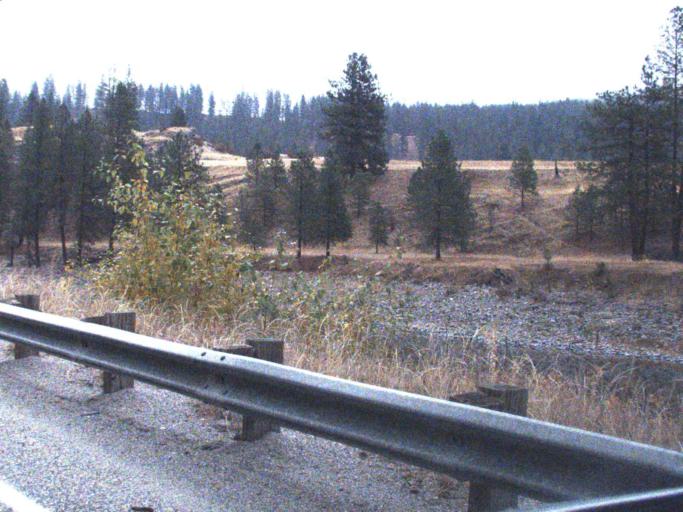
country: US
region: Washington
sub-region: Stevens County
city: Kettle Falls
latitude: 48.7958
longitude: -118.1610
